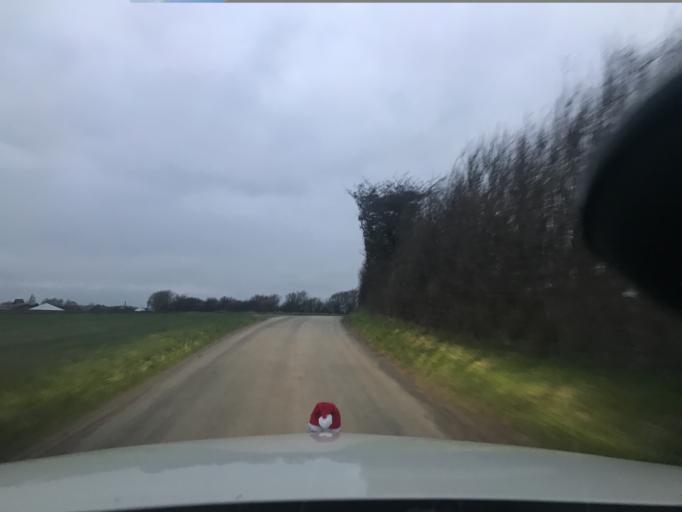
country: DK
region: South Denmark
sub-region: Sonderborg Kommune
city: Dybbol
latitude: 54.8549
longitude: 9.7317
